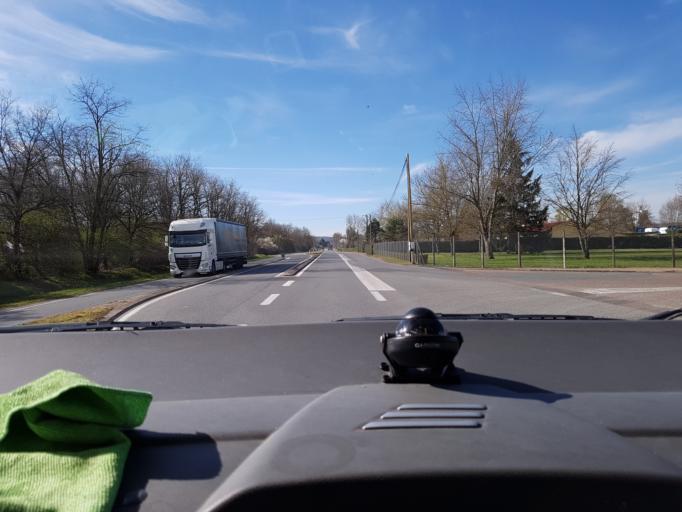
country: FR
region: Bourgogne
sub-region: Departement de Saone-et-Loire
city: Gueugnon
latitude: 46.5797
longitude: 4.0613
